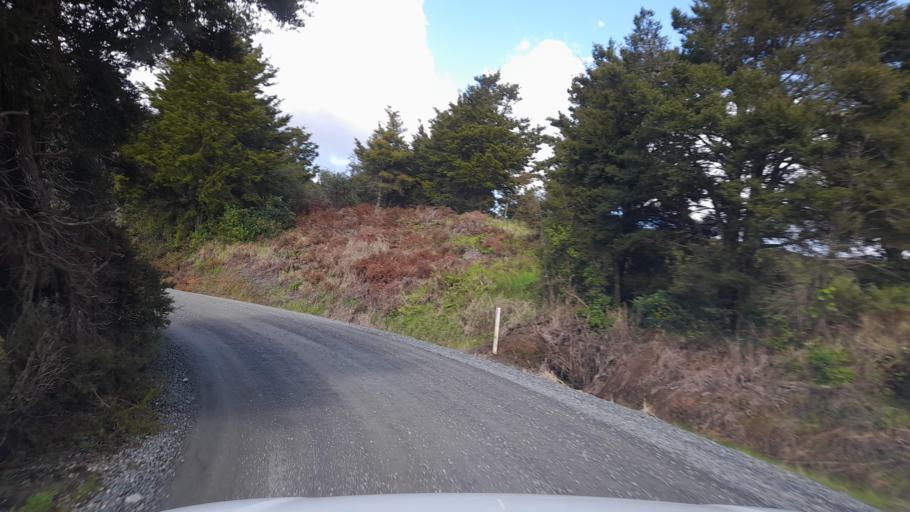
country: NZ
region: Northland
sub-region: Far North District
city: Kerikeri
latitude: -35.1298
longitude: 173.7400
